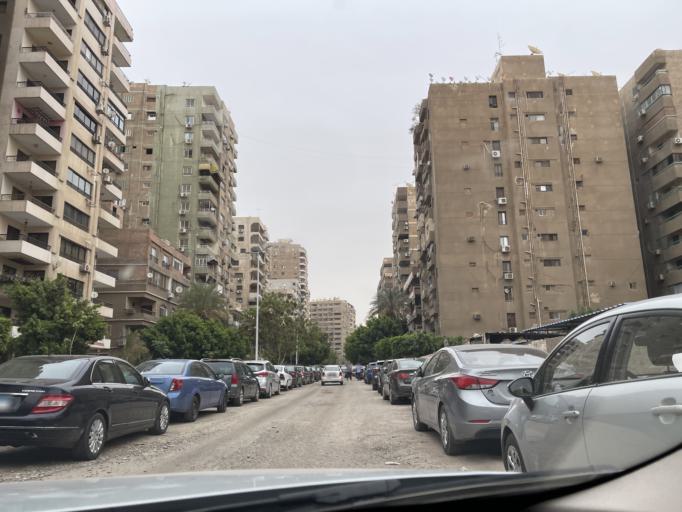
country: EG
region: Muhafazat al Qahirah
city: Cairo
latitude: 30.0603
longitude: 31.3539
